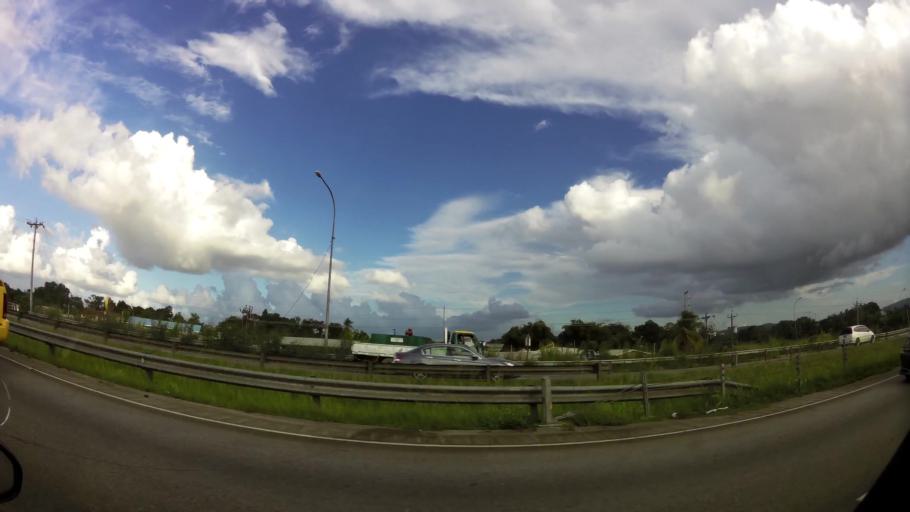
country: TT
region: Chaguanas
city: Chaguanas
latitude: 10.4609
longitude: -61.4105
